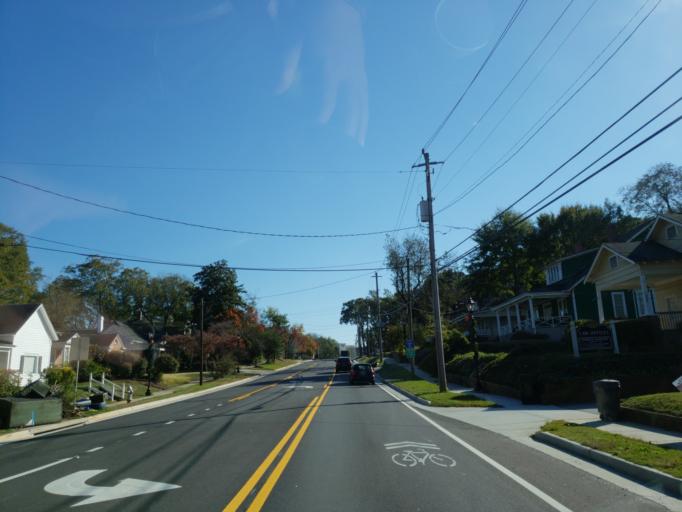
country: US
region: Georgia
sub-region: Gwinnett County
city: Lawrenceville
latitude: 33.9543
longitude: -83.9895
